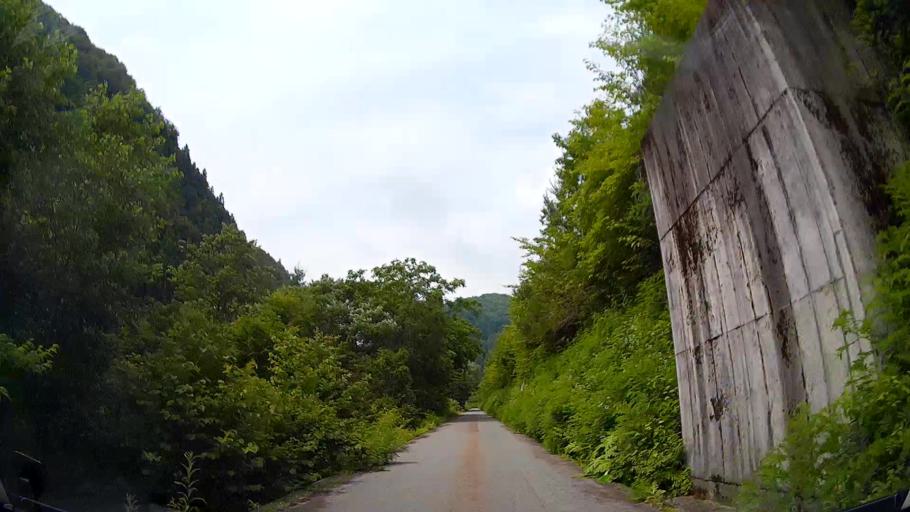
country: JP
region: Nagano
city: Iida
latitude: 35.4464
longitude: 137.9949
